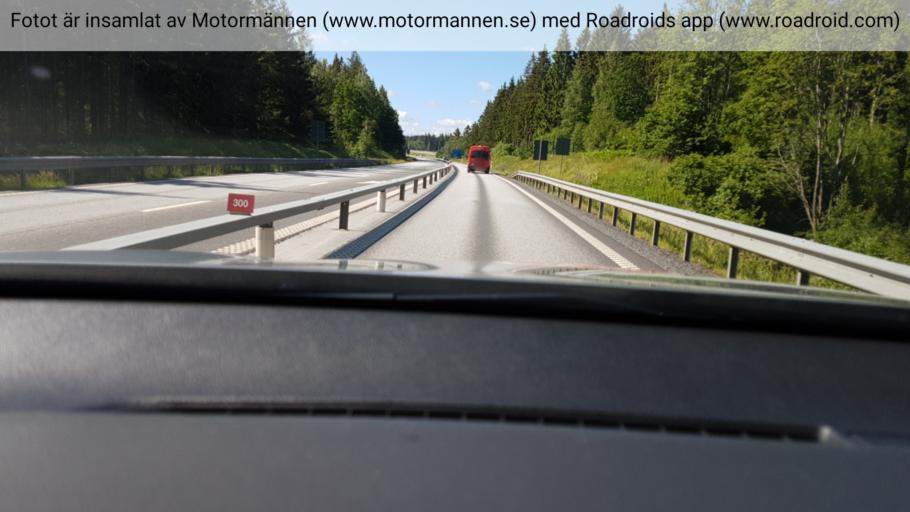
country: SE
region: Joenkoeping
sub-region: Jonkopings Kommun
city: Bankeryd
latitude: 57.8373
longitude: 14.1034
